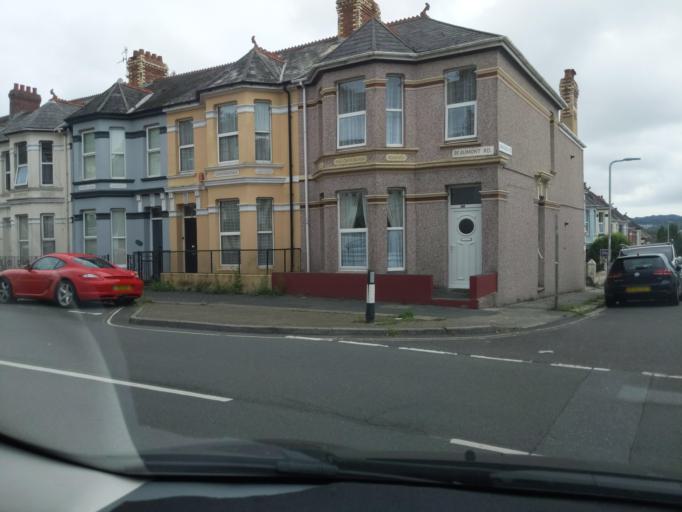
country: GB
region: England
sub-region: Plymouth
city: Plymouth
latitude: 50.3763
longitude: -4.1165
